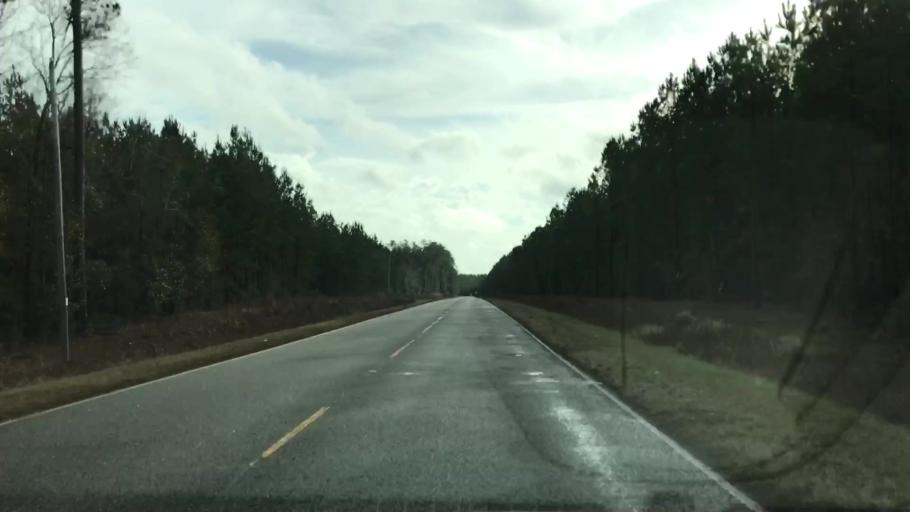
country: US
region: South Carolina
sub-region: Williamsburg County
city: Andrews
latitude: 33.4281
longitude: -79.5945
